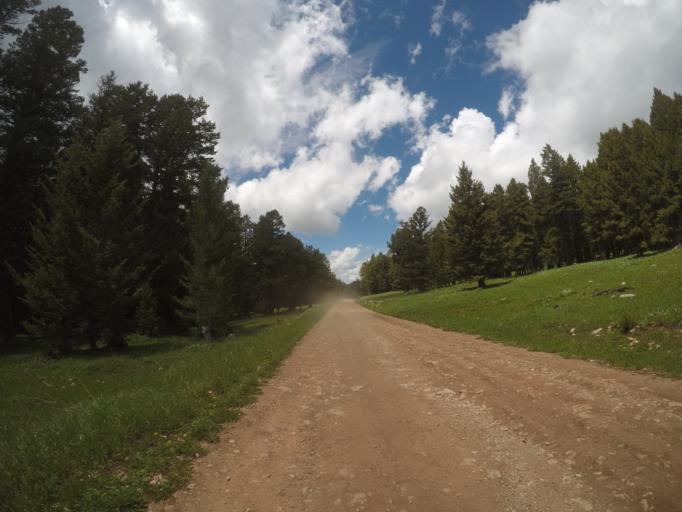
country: US
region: Wyoming
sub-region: Big Horn County
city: Lovell
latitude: 45.1638
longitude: -108.4059
